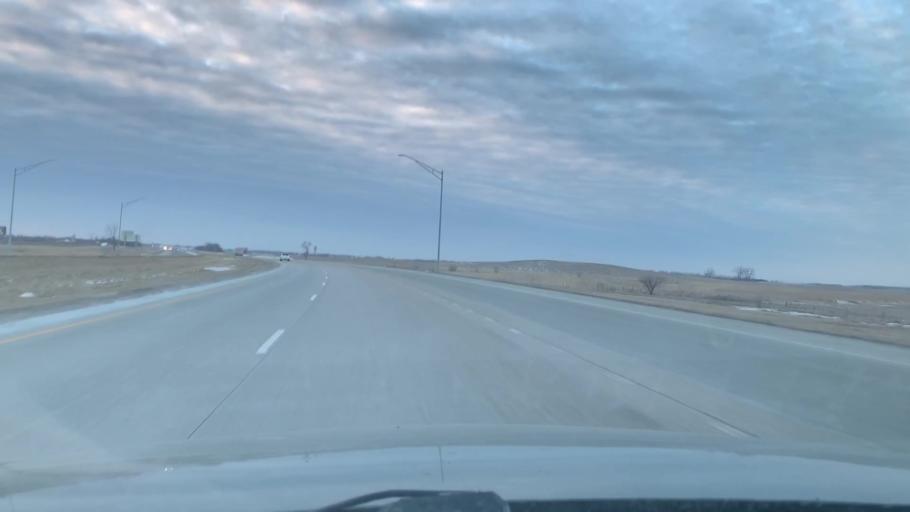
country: US
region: North Dakota
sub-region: Barnes County
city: Valley City
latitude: 46.9198
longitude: -97.6866
